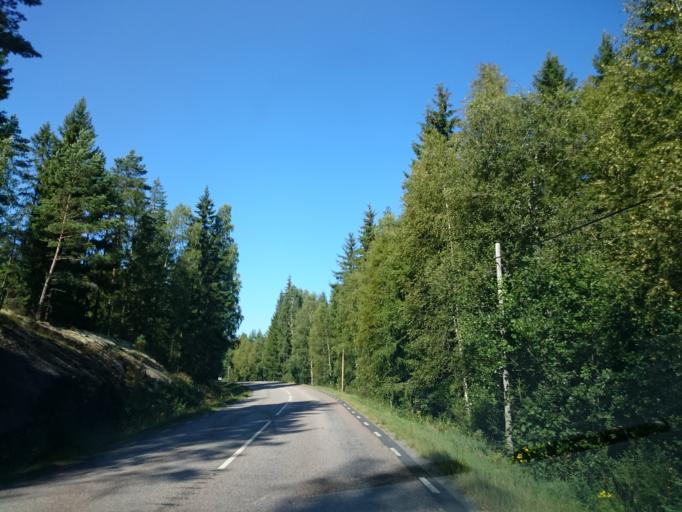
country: SE
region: OEstergoetland
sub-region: Norrkopings Kommun
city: Krokek
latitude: 58.6588
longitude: 16.5156
